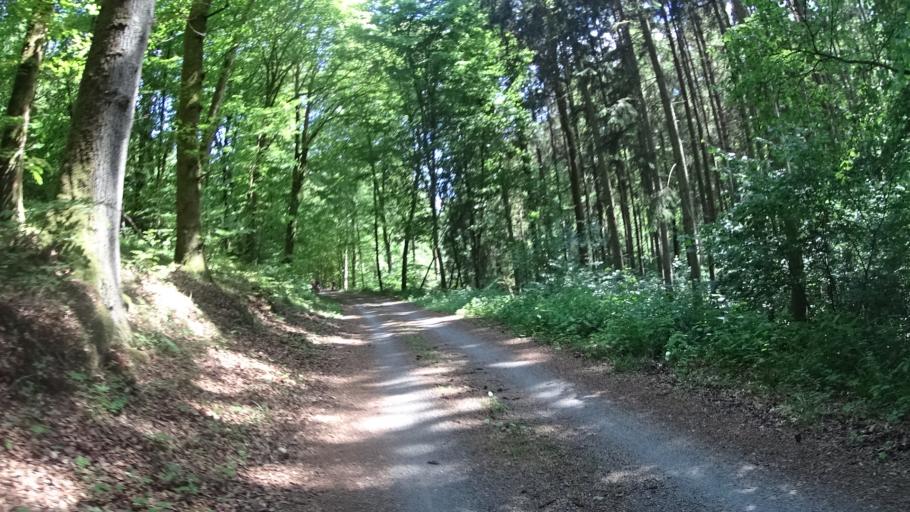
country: DE
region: Baden-Wuerttemberg
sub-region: Karlsruhe Region
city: Hopfingen
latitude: 49.6414
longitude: 9.4366
